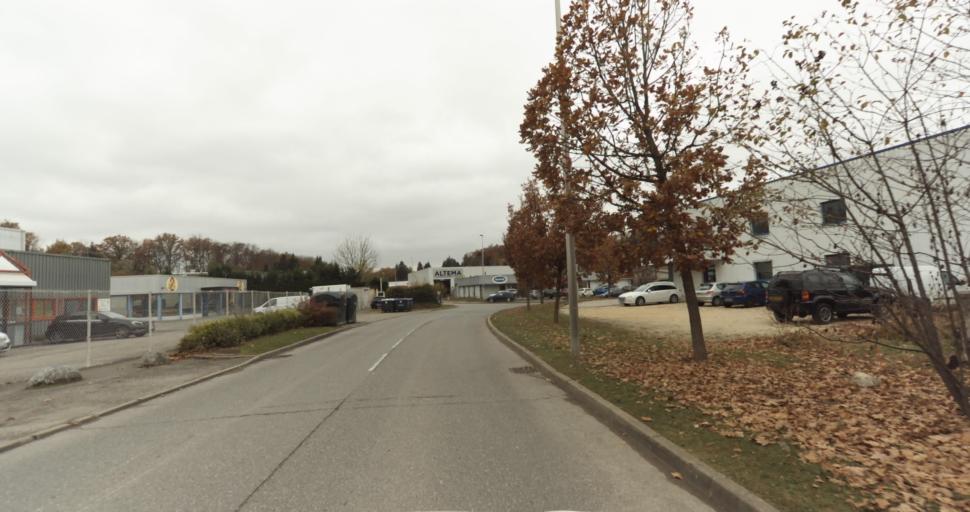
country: FR
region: Rhone-Alpes
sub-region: Departement de la Haute-Savoie
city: Seynod
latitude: 45.8853
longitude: 6.0740
